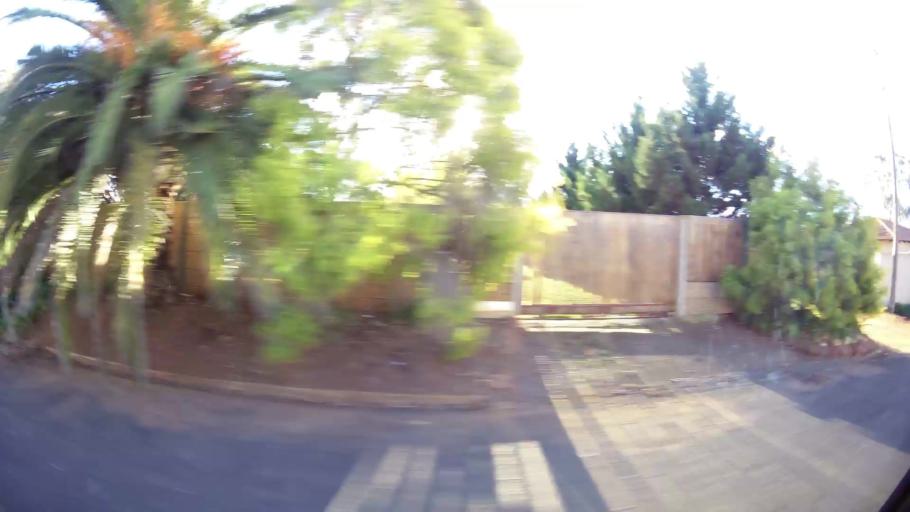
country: ZA
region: Western Cape
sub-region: Eden District Municipality
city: Riversdale
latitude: -34.0938
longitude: 20.9542
